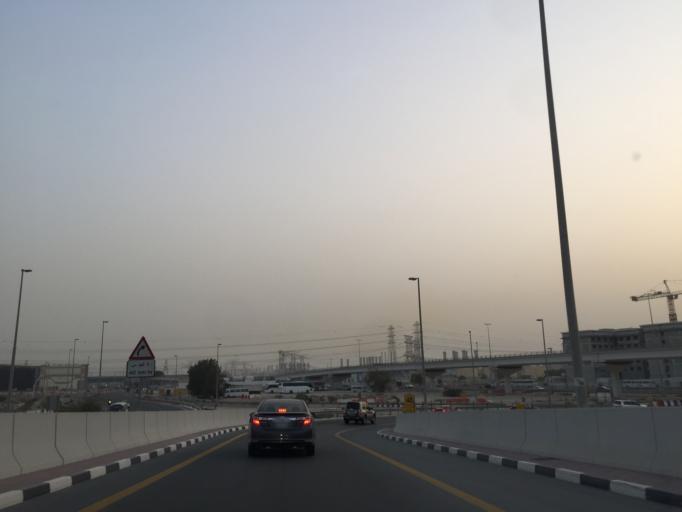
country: AE
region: Dubai
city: Dubai
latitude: 25.0631
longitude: 55.1335
